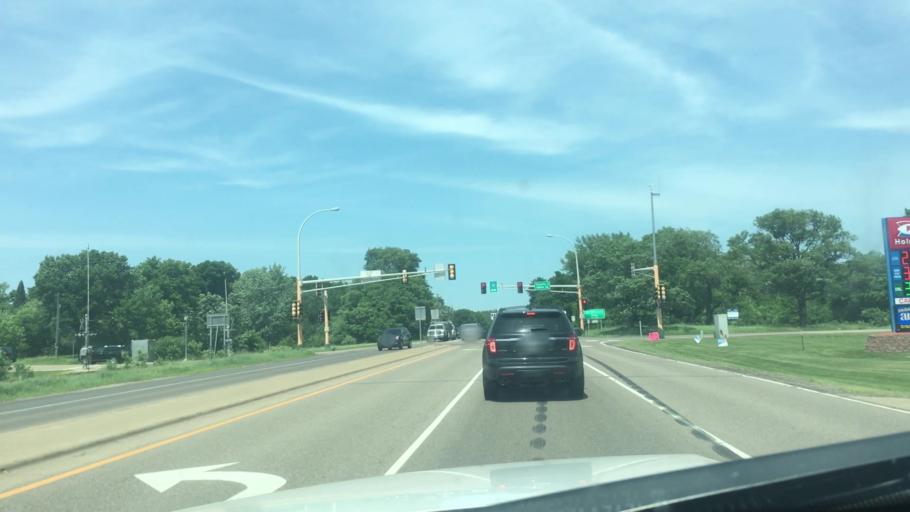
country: US
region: Minnesota
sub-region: Washington County
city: Hugo
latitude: 45.1230
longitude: -93.0031
